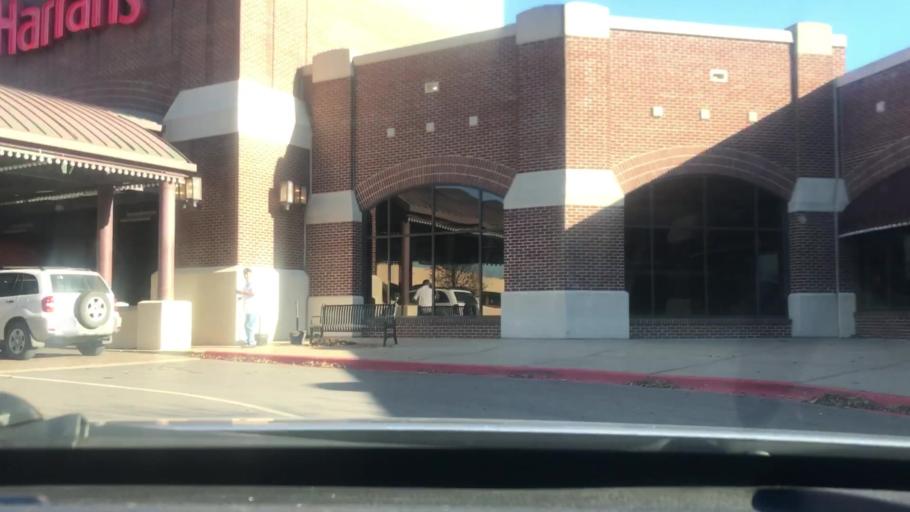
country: US
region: Missouri
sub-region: Clay County
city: North Kansas City
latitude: 39.1423
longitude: -94.5446
